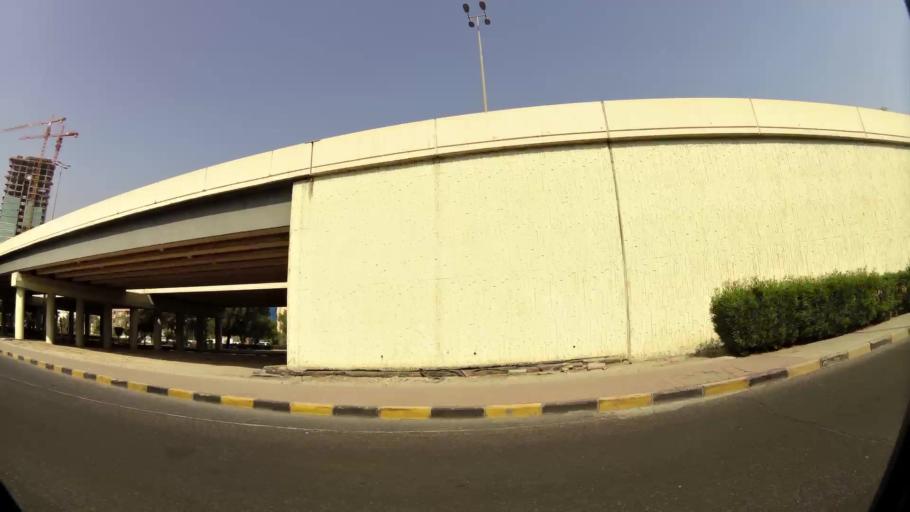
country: KW
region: Al Asimah
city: Ad Dasmah
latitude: 29.3651
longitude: 48.0116
